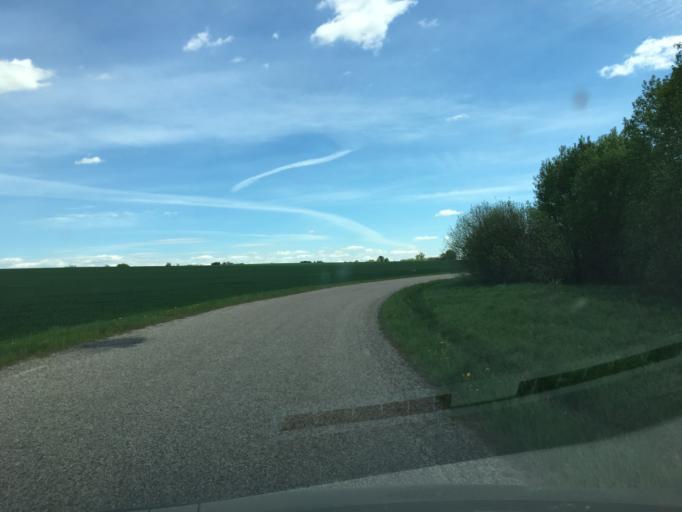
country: EE
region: Vorumaa
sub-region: Antsla vald
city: Vana-Antsla
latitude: 57.9150
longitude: 26.3397
